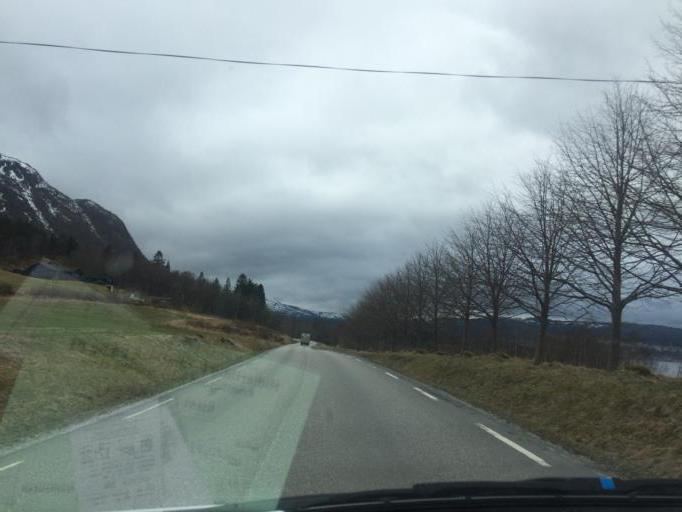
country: NO
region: More og Romsdal
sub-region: Gjemnes
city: Batnfjordsora
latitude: 62.9644
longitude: 7.7631
